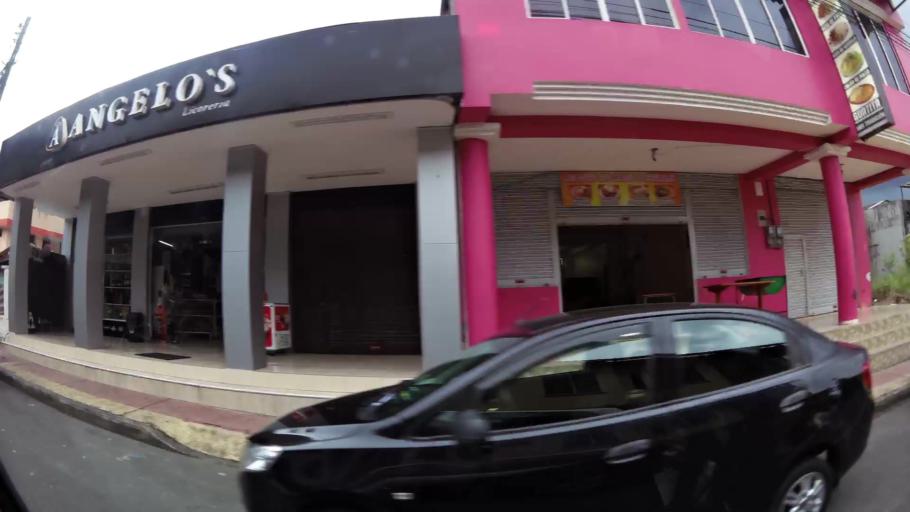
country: EC
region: Pastaza
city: Puyo
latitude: -1.4907
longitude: -78.0001
